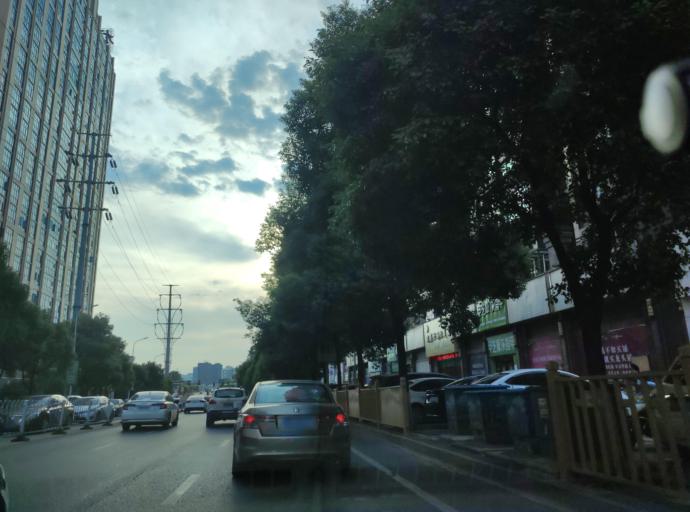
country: CN
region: Jiangxi Sheng
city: Pingxiang
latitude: 27.6338
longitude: 113.8656
